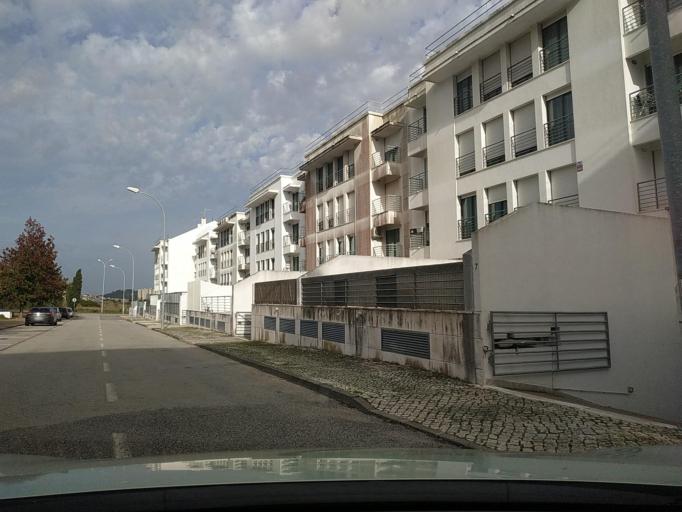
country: PT
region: Lisbon
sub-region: Odivelas
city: Famoes
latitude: 38.7834
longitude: -9.2329
